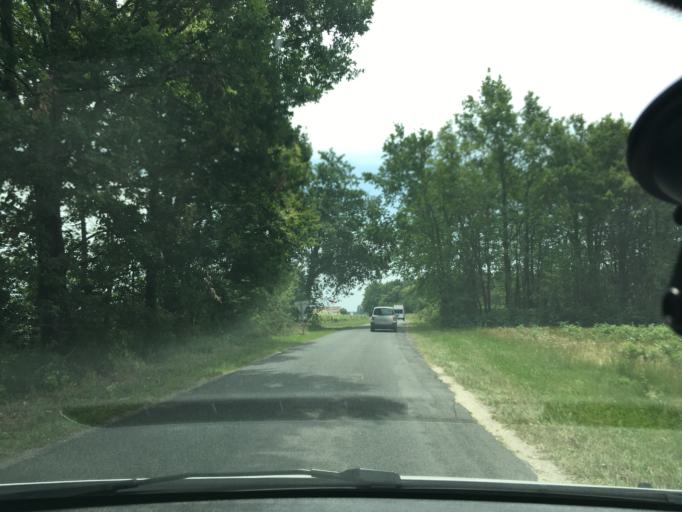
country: FR
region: Aquitaine
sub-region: Departement de la Gironde
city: Castelnau-de-Medoc
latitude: 45.0451
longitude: -0.8064
